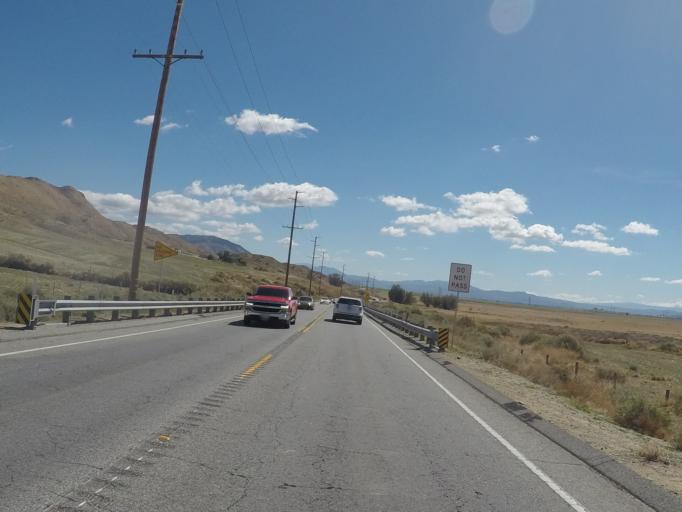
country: US
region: California
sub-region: Riverside County
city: Lakeview
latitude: 33.8823
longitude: -117.0599
